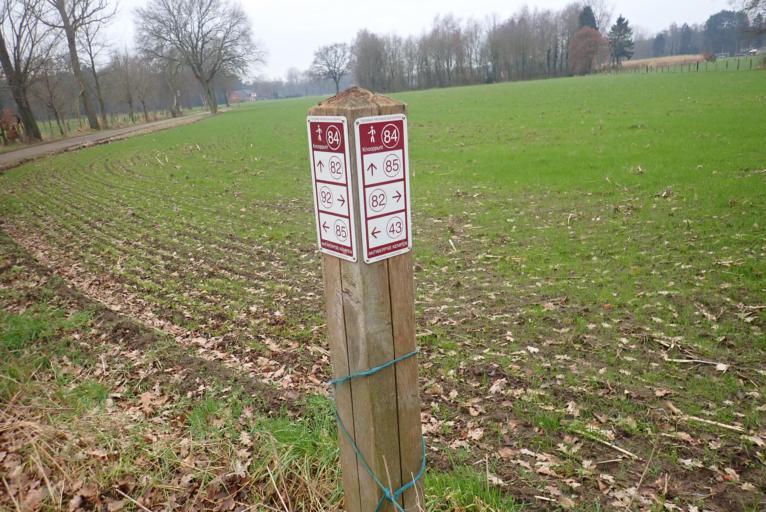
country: BE
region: Flanders
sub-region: Provincie Antwerpen
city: Vorselaar
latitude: 51.2248
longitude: 4.7616
